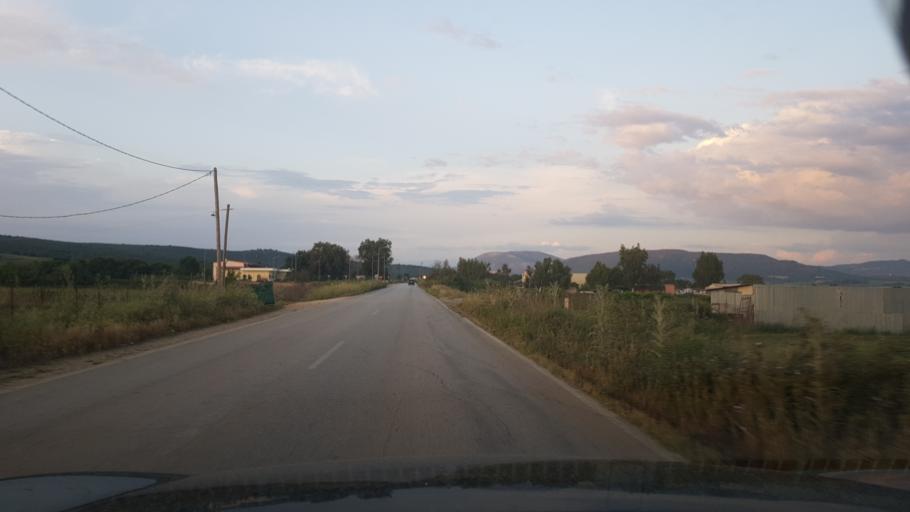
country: GR
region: West Greece
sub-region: Nomos Aitolias kai Akarnanias
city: Vonitsa
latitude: 38.8736
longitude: 20.8149
